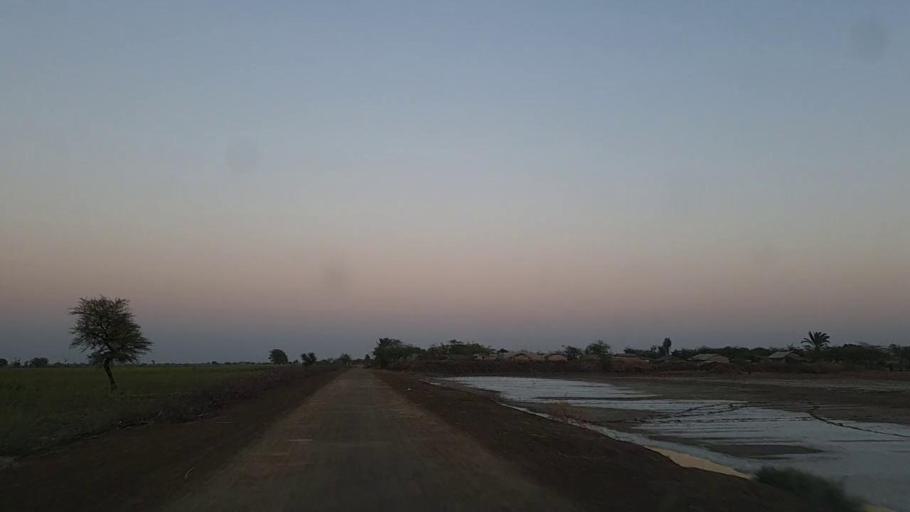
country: PK
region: Sindh
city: Samaro
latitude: 25.3251
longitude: 69.4028
